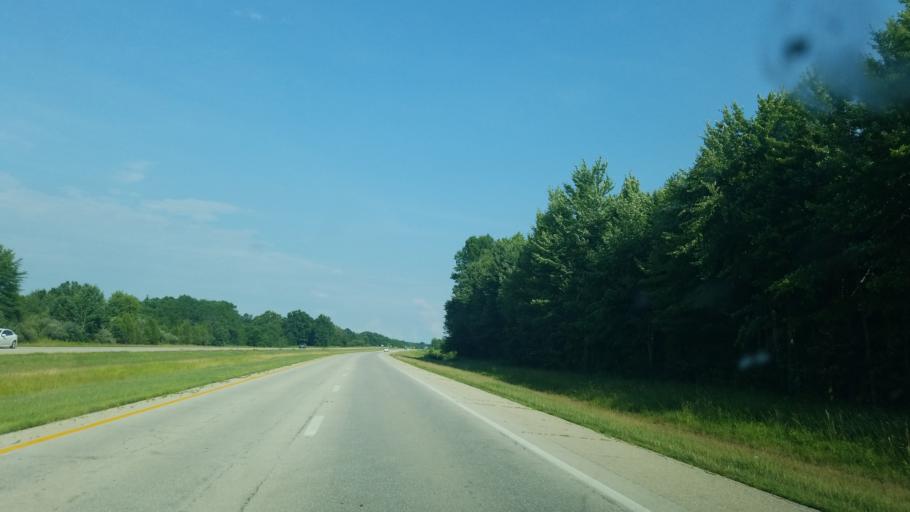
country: US
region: Ohio
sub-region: Brown County
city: Mount Orab
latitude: 39.0302
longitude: -83.8874
